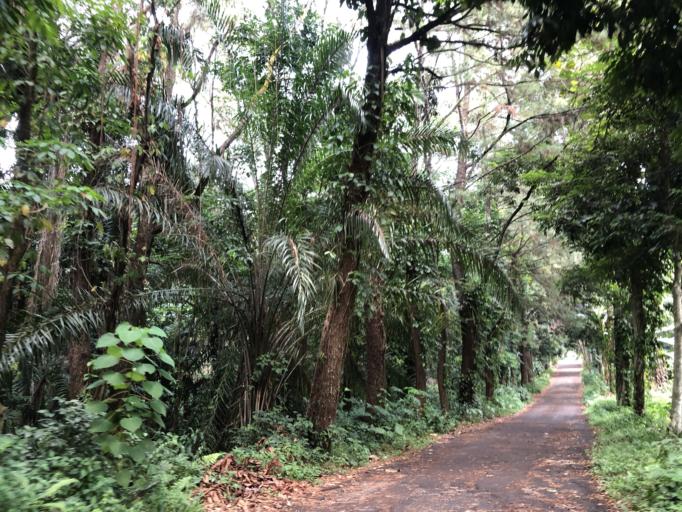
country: ID
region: West Java
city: Ciampea
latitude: -6.5559
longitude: 106.7231
